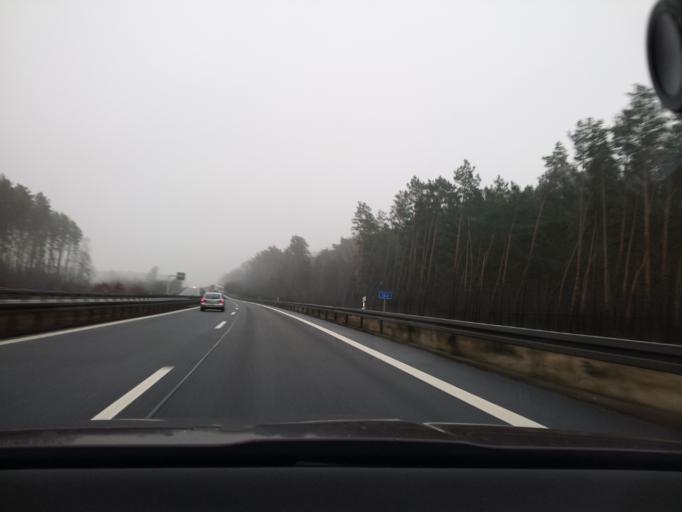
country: DE
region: Brandenburg
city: Storkow
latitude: 52.3131
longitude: 13.9216
